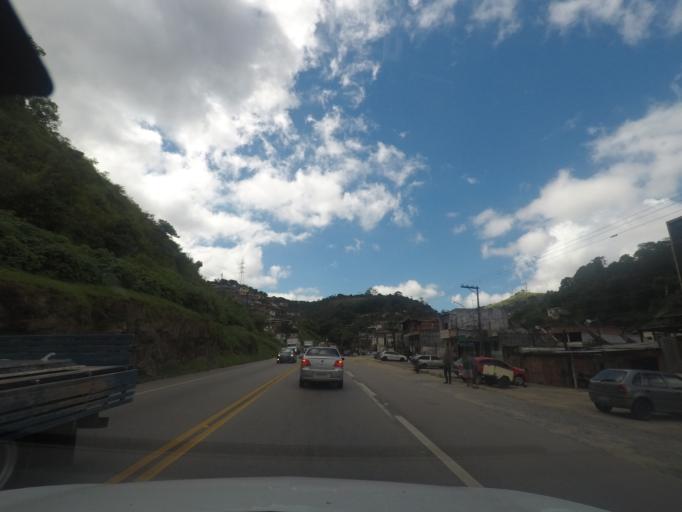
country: BR
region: Rio de Janeiro
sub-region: Teresopolis
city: Teresopolis
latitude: -22.3927
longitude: -42.9530
